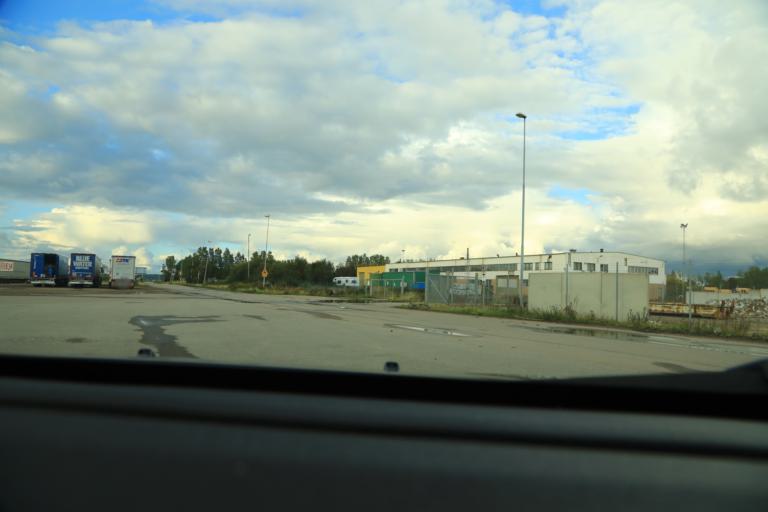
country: SE
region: Halland
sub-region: Varbergs Kommun
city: Varberg
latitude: 57.1187
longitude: 12.2429
